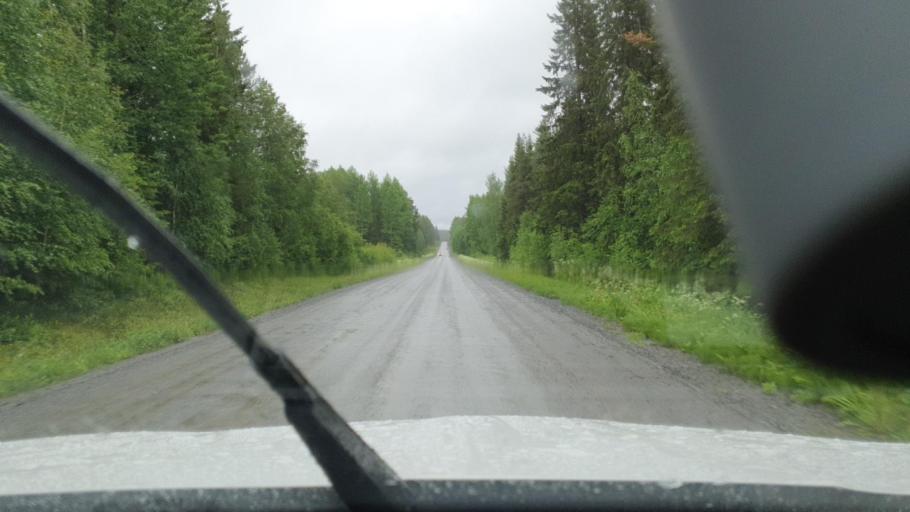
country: SE
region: Vaesterbotten
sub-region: Skelleftea Kommun
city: Burtraesk
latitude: 64.3831
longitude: 20.3203
